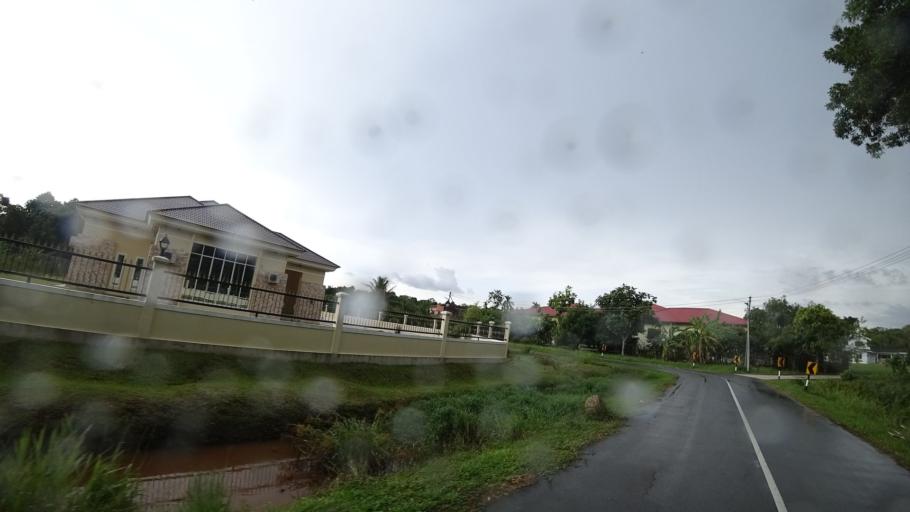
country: MY
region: Sarawak
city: Limbang
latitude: 4.8261
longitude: 114.9081
